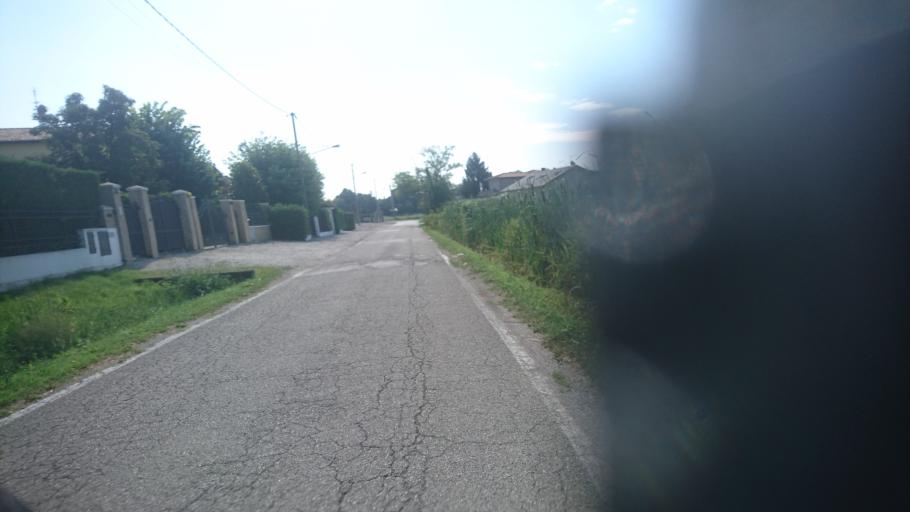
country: IT
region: Veneto
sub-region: Provincia di Padova
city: Mandriola-Sant'Agostino
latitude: 45.3735
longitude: 11.8380
